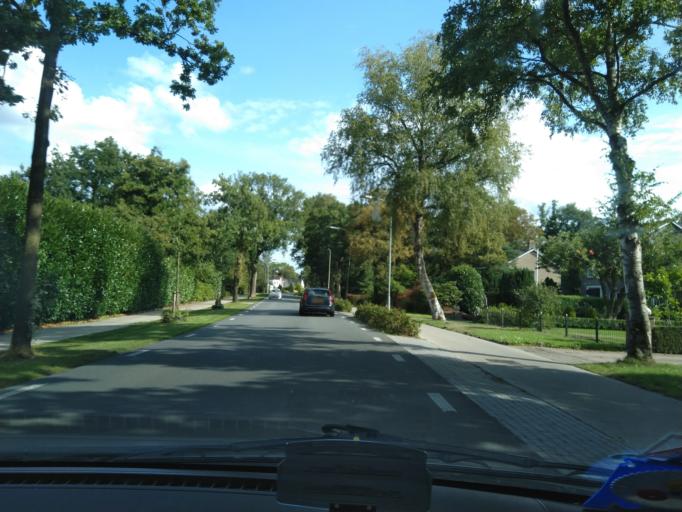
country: NL
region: Groningen
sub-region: Gemeente Groningen
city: Groningen
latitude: 53.1702
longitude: 6.5498
